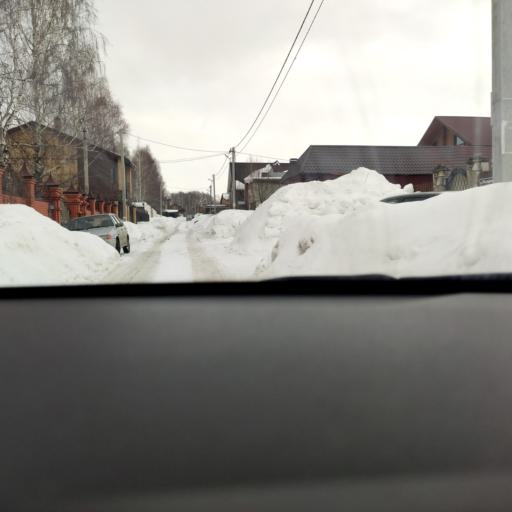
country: RU
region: Tatarstan
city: Vysokaya Gora
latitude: 55.8077
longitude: 49.2793
